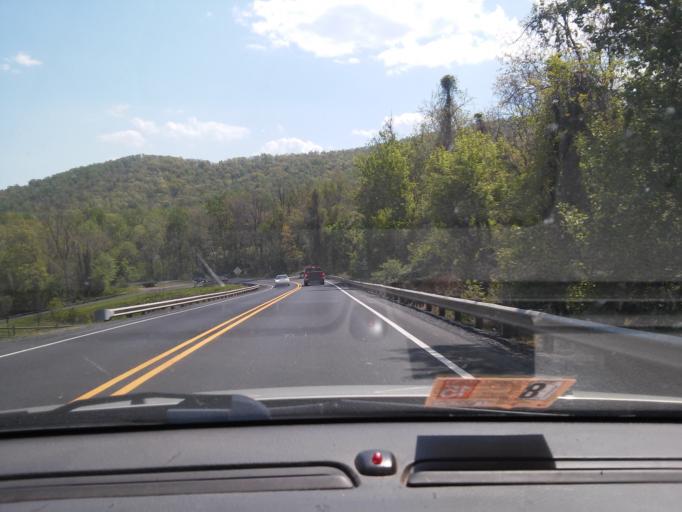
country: US
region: Virginia
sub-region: Warren County
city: Apple Mountain Lake
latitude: 38.8455
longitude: -78.1251
